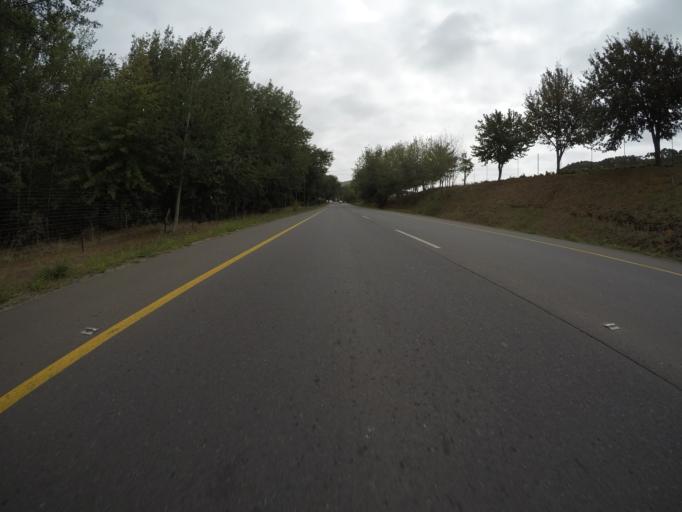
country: ZA
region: Western Cape
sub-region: City of Cape Town
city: Sunset Beach
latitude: -33.8389
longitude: 18.6025
